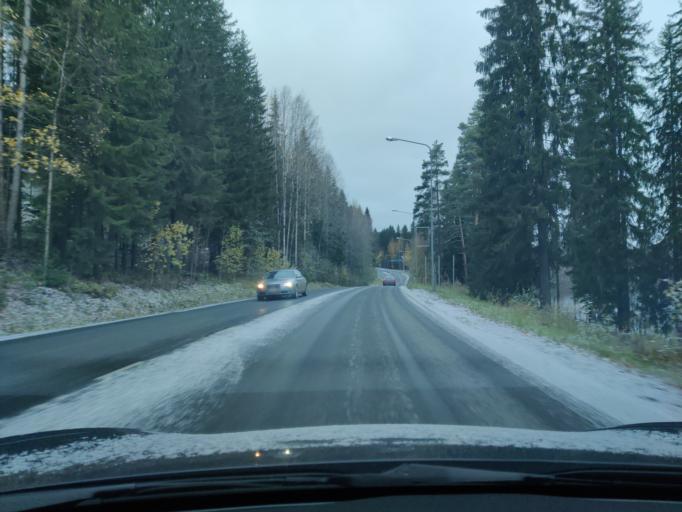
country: FI
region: Northern Savo
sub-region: Kuopio
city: Kuopio
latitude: 62.8427
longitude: 27.6323
